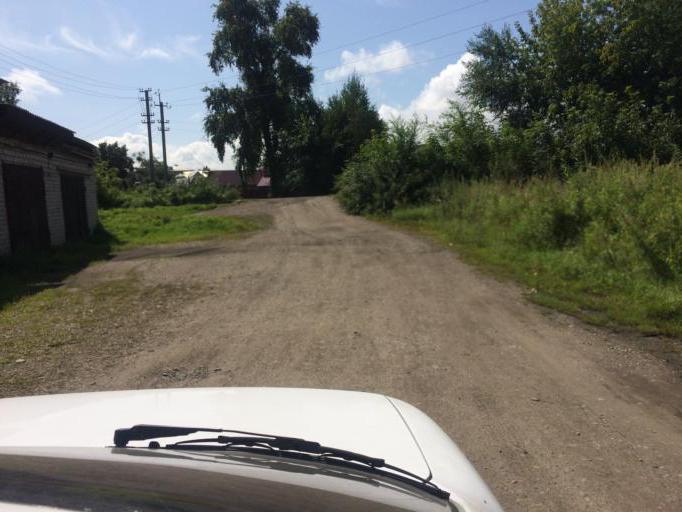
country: RU
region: Primorskiy
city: Dal'nerechensk
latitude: 45.9390
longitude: 133.7336
